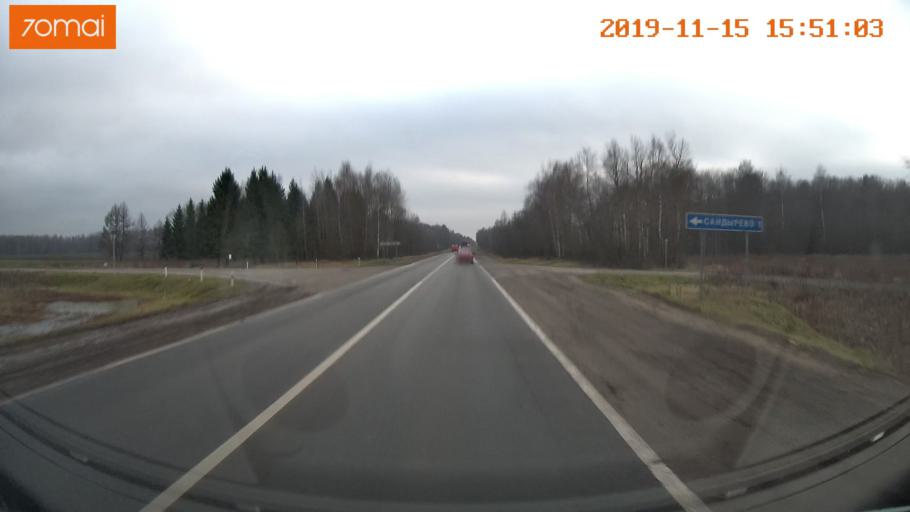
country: RU
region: Jaroslavl
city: Yaroslavl
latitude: 57.8991
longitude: 40.0104
